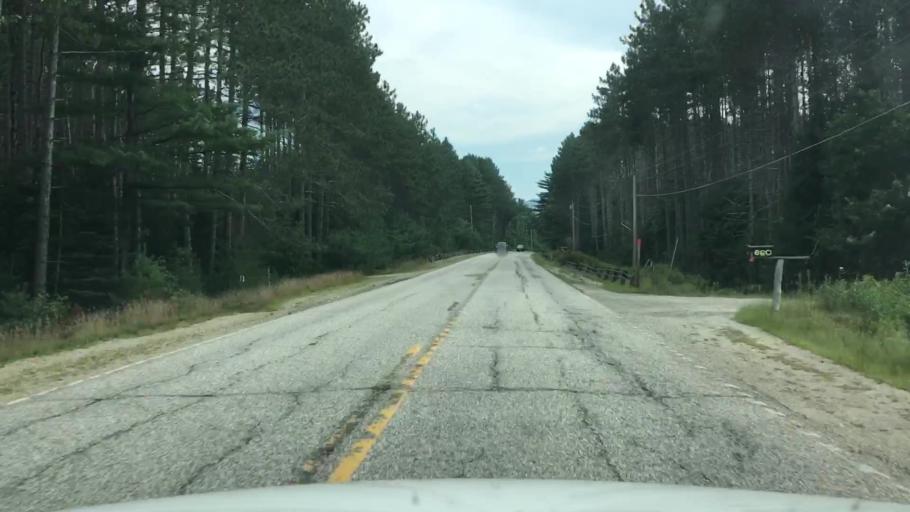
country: US
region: Maine
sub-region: Oxford County
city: Rumford
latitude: 44.6075
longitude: -70.7359
